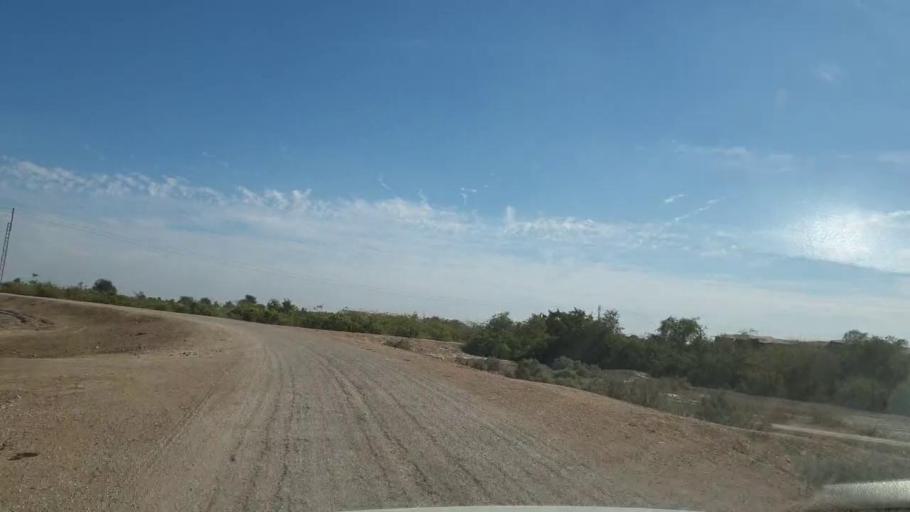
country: PK
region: Sindh
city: Pithoro
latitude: 25.5806
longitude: 69.2896
